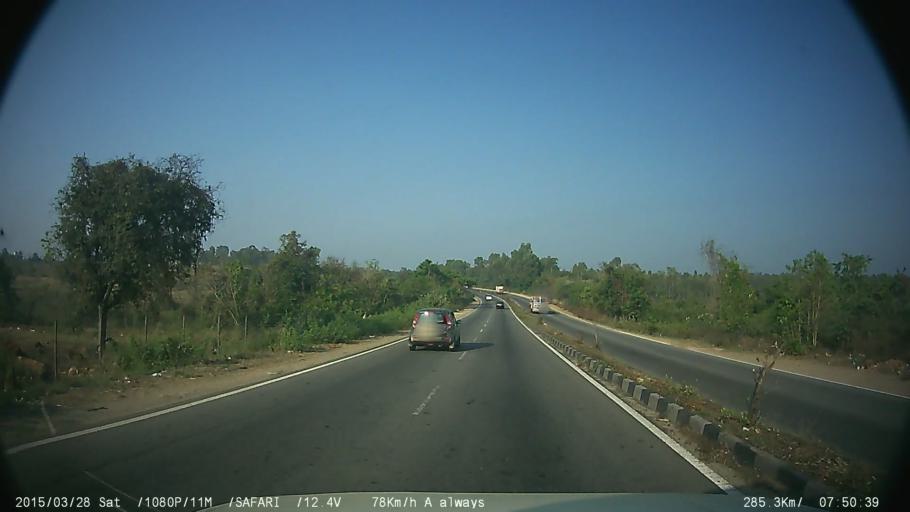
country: IN
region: Karnataka
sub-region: Mandya
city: Shrirangapattana
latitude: 12.4659
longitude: 76.7507
